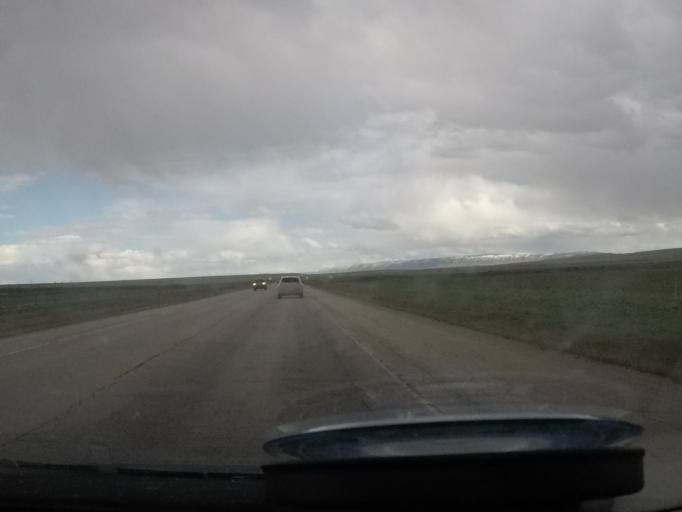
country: US
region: Wyoming
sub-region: Natrona County
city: Mills
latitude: 42.9519
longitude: -106.6374
